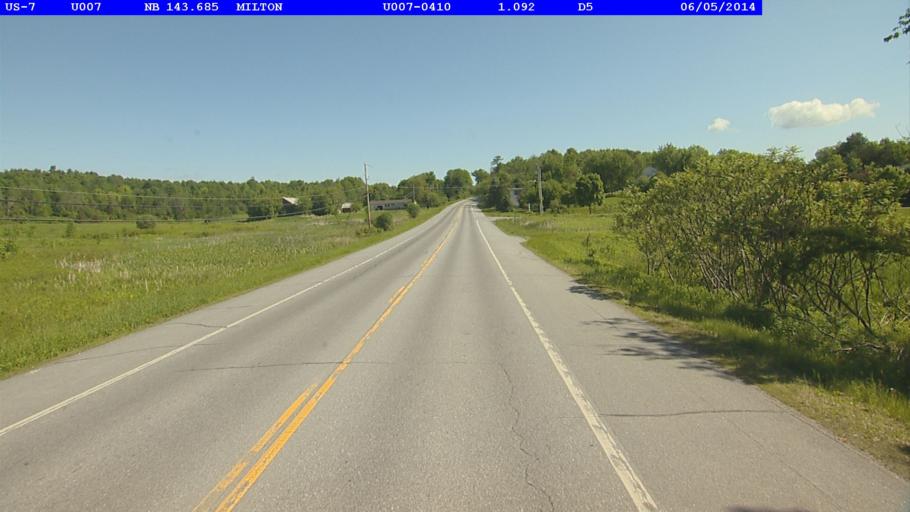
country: US
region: Vermont
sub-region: Chittenden County
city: Milton
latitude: 44.6098
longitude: -73.1553
